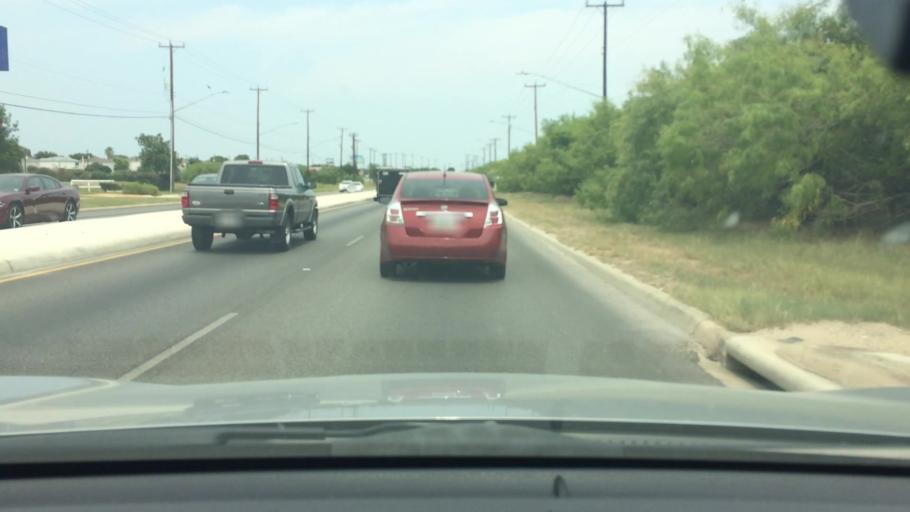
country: US
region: Texas
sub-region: Bexar County
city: Leon Valley
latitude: 29.4898
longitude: -98.6897
